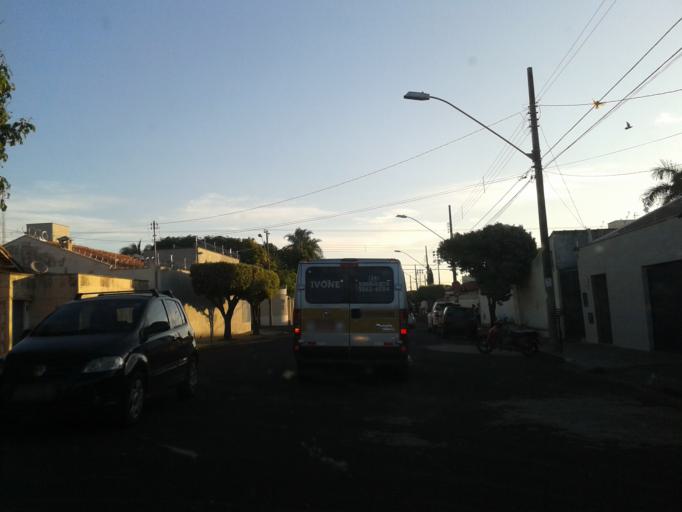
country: BR
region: Minas Gerais
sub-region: Ituiutaba
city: Ituiutaba
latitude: -18.9833
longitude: -49.4584
